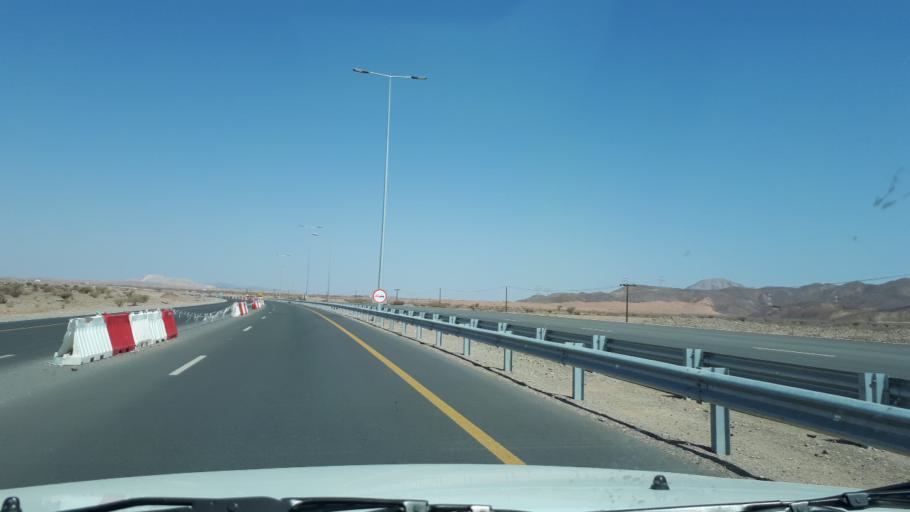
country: OM
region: Ash Sharqiyah
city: Badiyah
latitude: 22.4905
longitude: 58.9711
